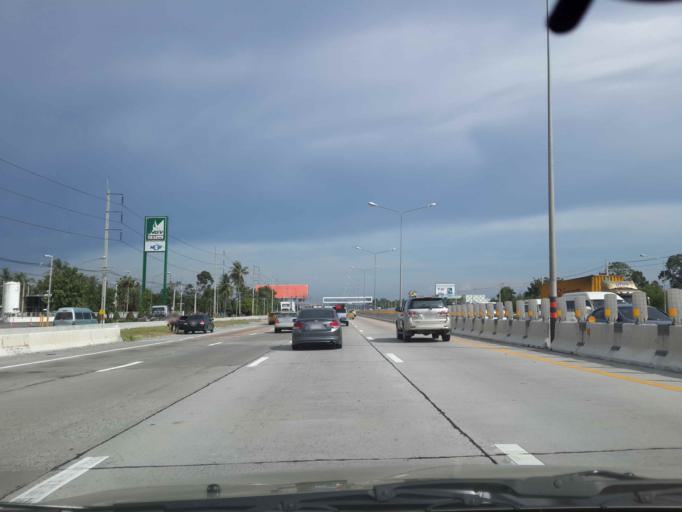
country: TH
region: Chon Buri
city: Si Racha
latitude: 13.2265
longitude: 101.0024
